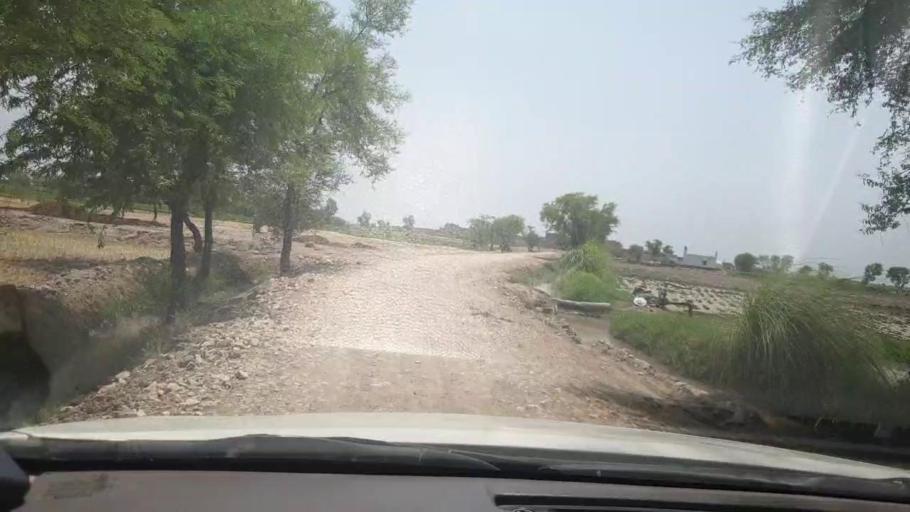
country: PK
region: Sindh
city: Garhi Yasin
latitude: 27.9135
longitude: 68.5572
